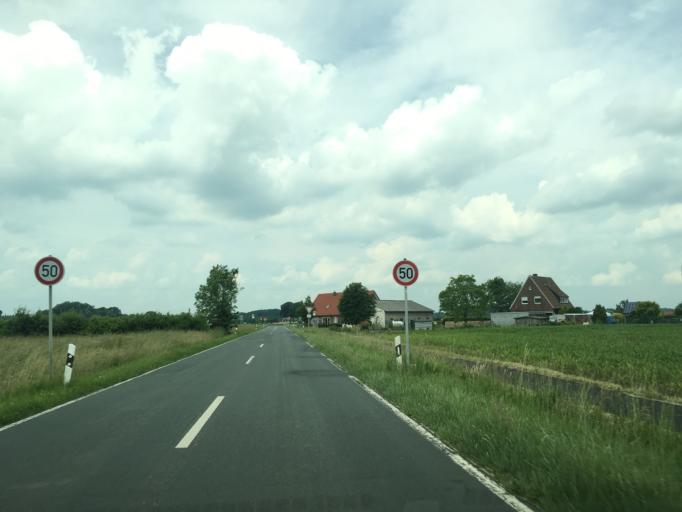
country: DE
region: North Rhine-Westphalia
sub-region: Regierungsbezirk Munster
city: Havixbeck
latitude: 52.0069
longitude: 7.3767
